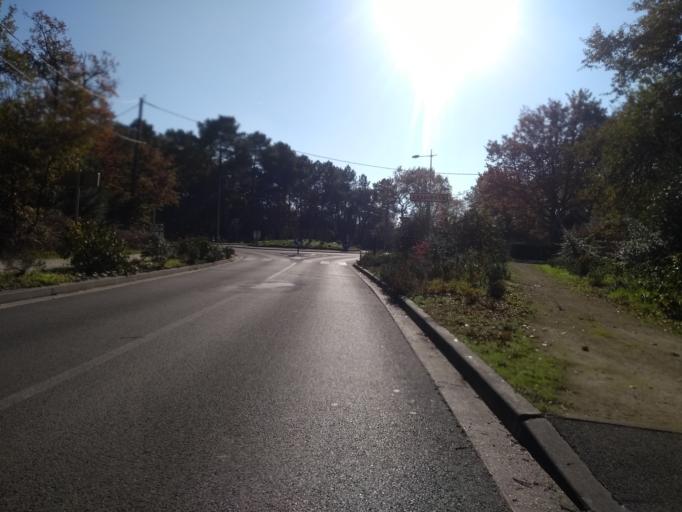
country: FR
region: Aquitaine
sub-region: Departement de la Gironde
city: Gradignan
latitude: 44.7492
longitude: -0.6167
